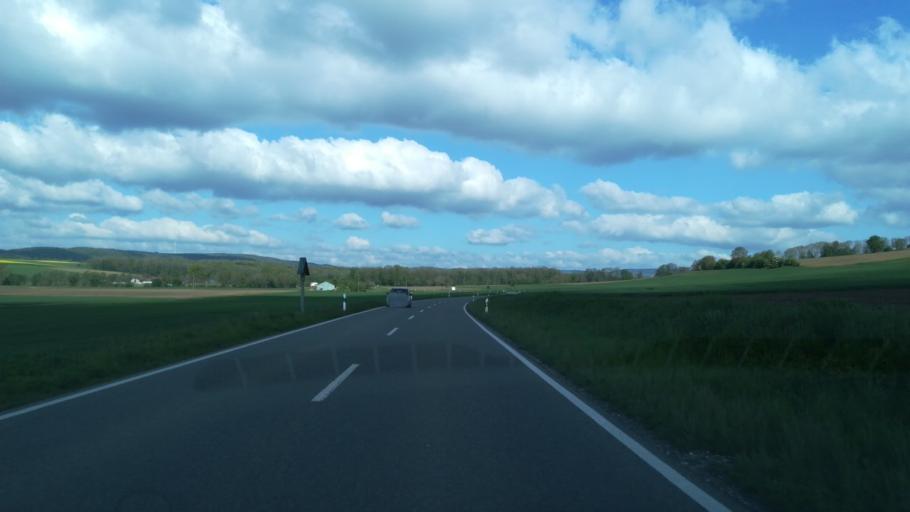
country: CH
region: Schaffhausen
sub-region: Bezirk Reiat
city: Thayngen
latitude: 47.7659
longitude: 8.7399
